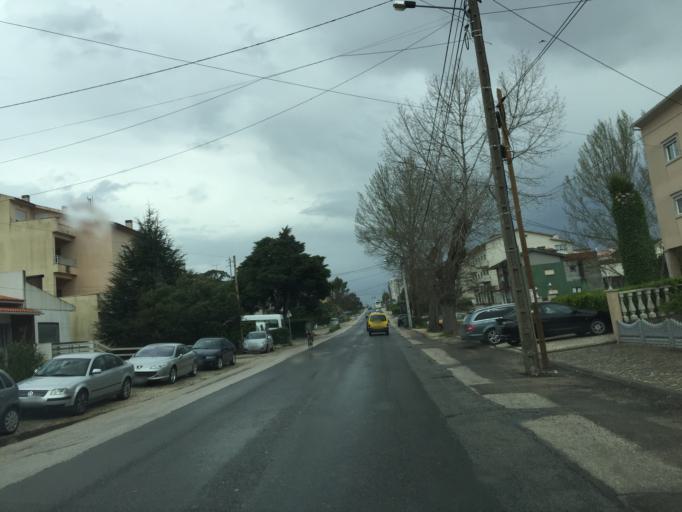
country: PT
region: Santarem
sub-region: Ourem
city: Fatima
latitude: 39.6372
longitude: -8.6844
